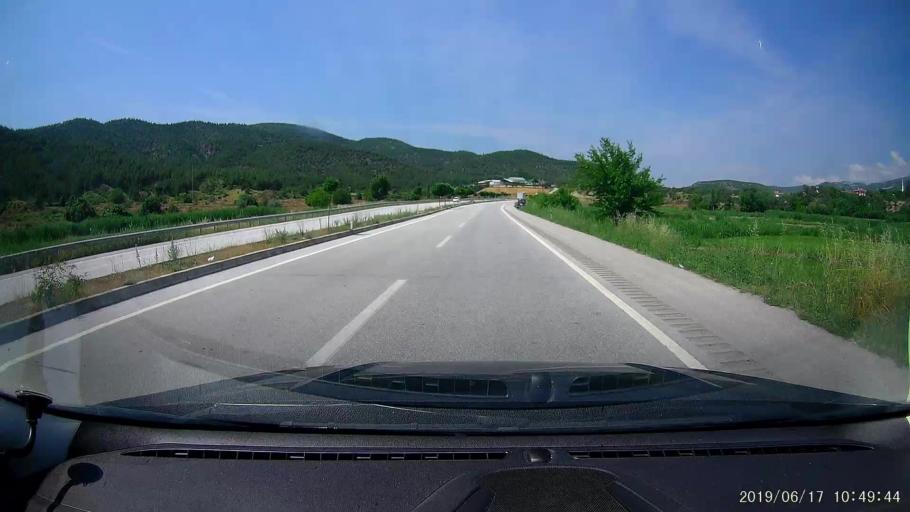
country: TR
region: Corum
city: Hacihamza
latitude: 41.0999
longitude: 34.4025
